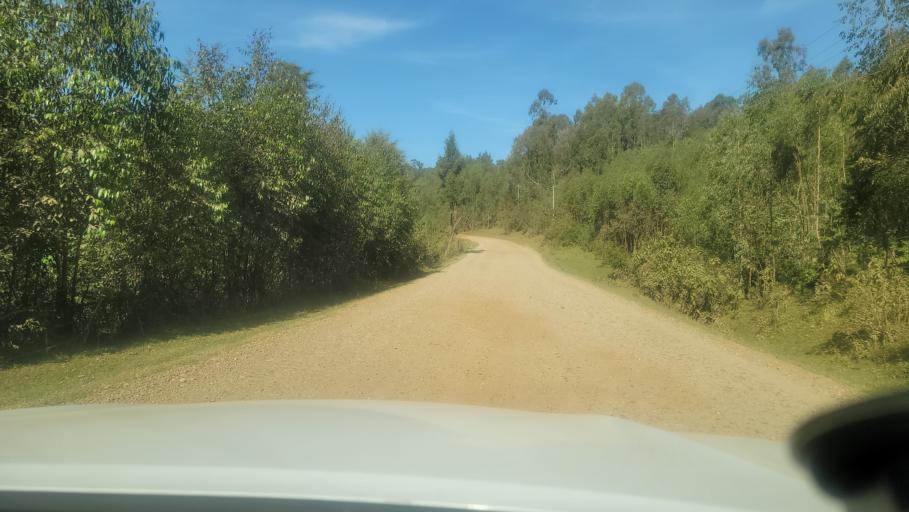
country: ET
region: Oromiya
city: Agaro
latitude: 7.8000
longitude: 36.4711
